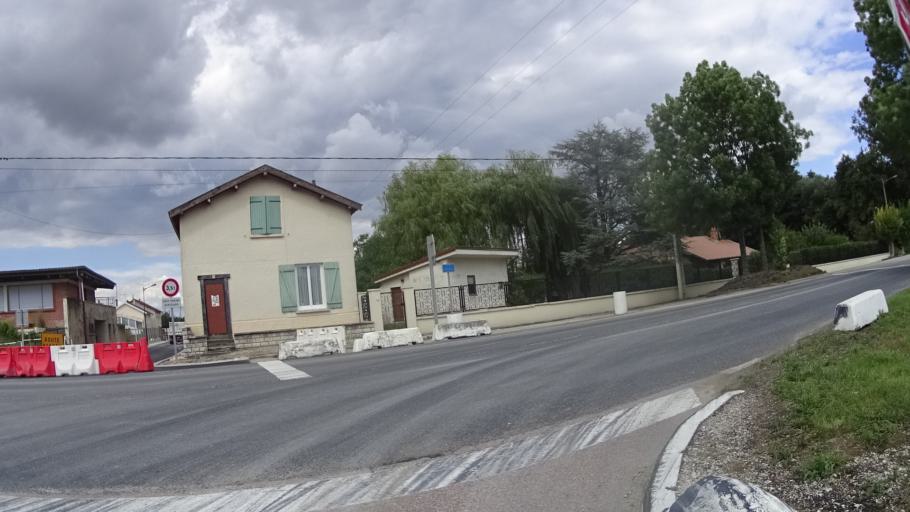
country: FR
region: Champagne-Ardenne
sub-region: Departement de la Haute-Marne
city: Villiers-en-Lieu
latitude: 48.6543
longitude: 4.8281
